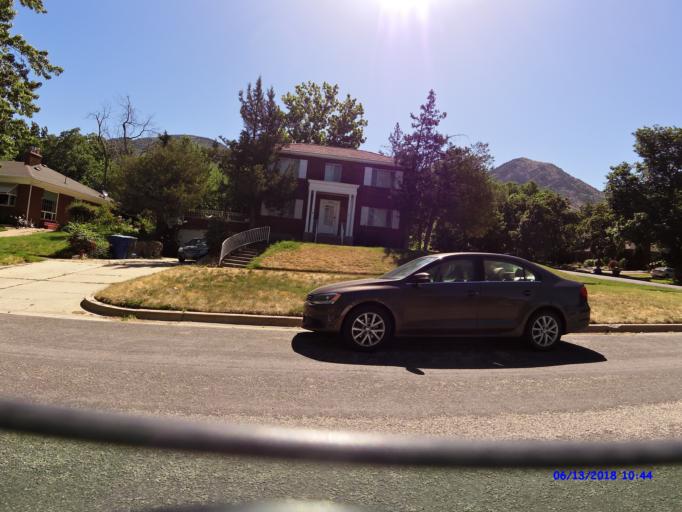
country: US
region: Utah
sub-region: Weber County
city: Ogden
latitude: 41.2184
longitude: -111.9400
